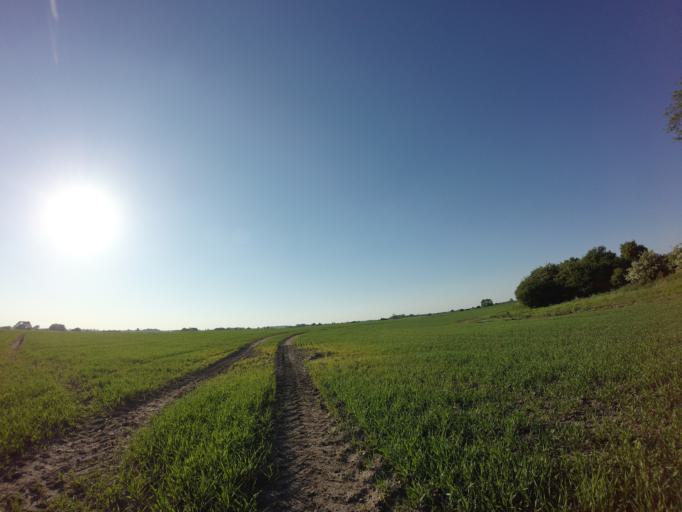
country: PL
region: West Pomeranian Voivodeship
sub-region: Powiat choszczenski
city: Choszczno
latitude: 53.1312
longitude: 15.4320
